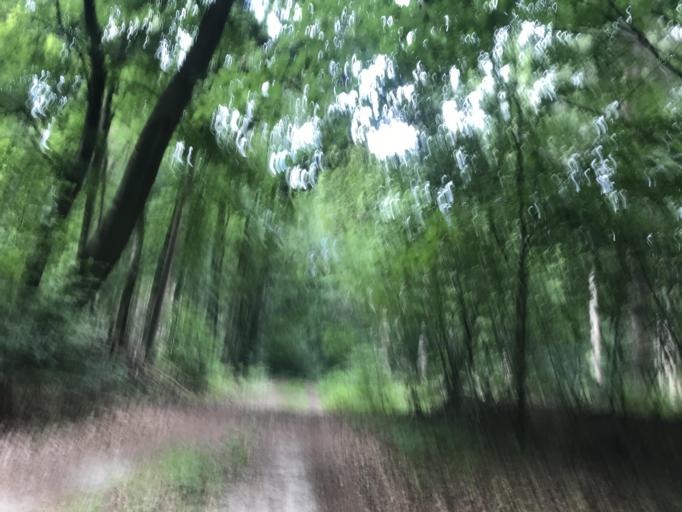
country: DE
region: Lower Saxony
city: Barendorf
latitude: 53.2374
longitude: 10.5330
